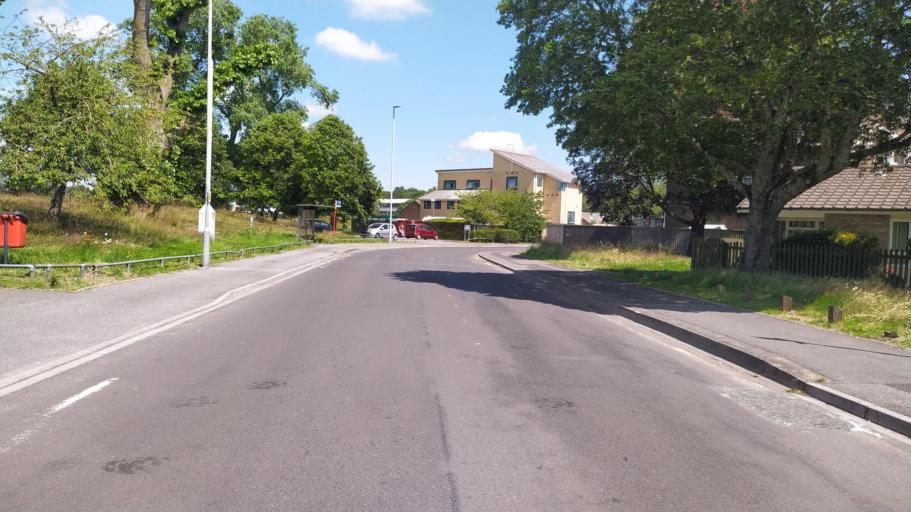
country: GB
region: England
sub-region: Poole
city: Poole
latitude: 50.7274
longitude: -2.0195
